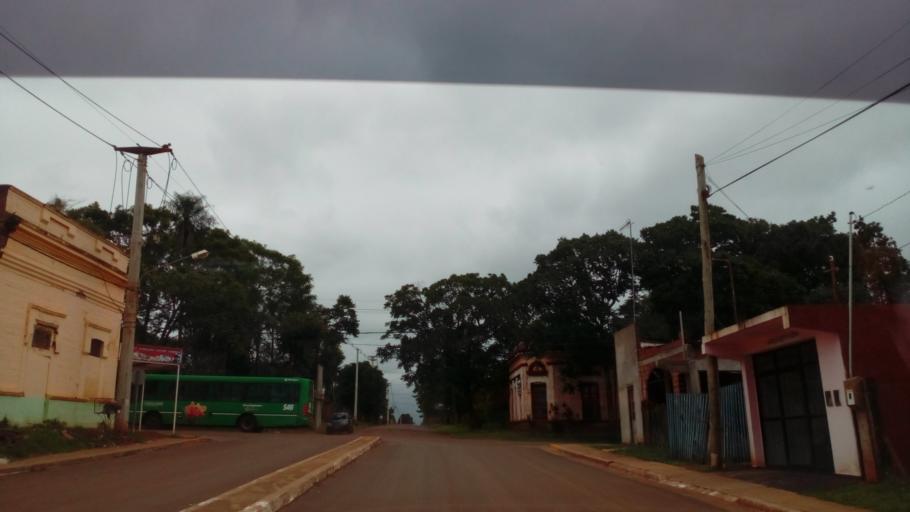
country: AR
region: Misiones
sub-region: Departamento de Candelaria
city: Candelaria
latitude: -27.4599
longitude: -55.7485
